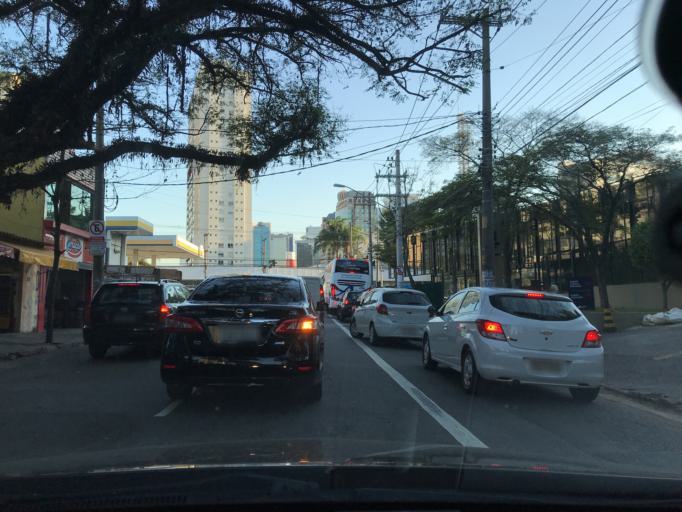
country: BR
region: Sao Paulo
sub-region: Sao Paulo
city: Sao Paulo
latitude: -23.6185
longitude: -46.6963
